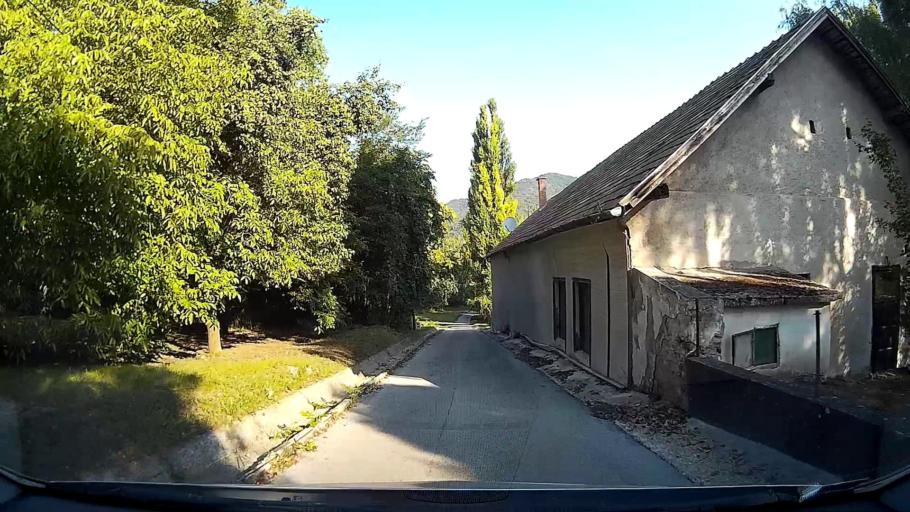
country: HU
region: Pest
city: Nagymaros
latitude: 47.7593
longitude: 18.9394
